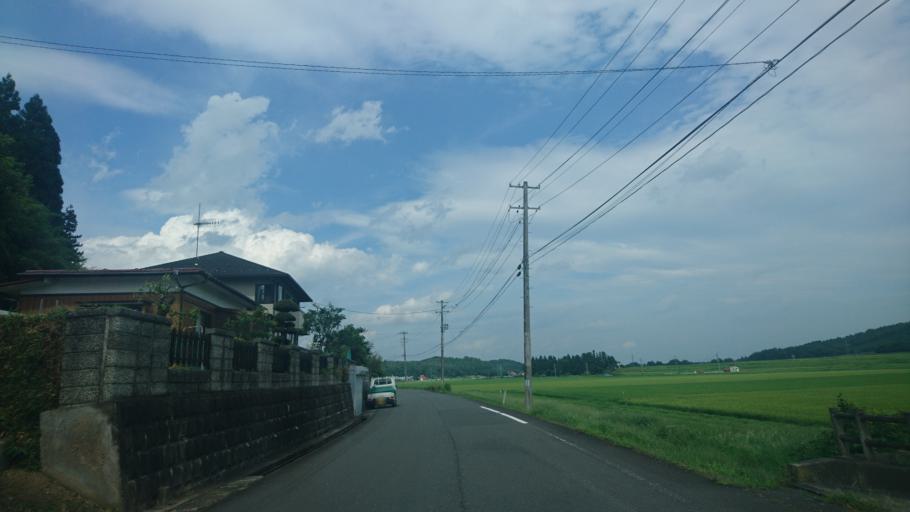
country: JP
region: Miyagi
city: Furukawa
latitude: 38.7651
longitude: 140.9842
